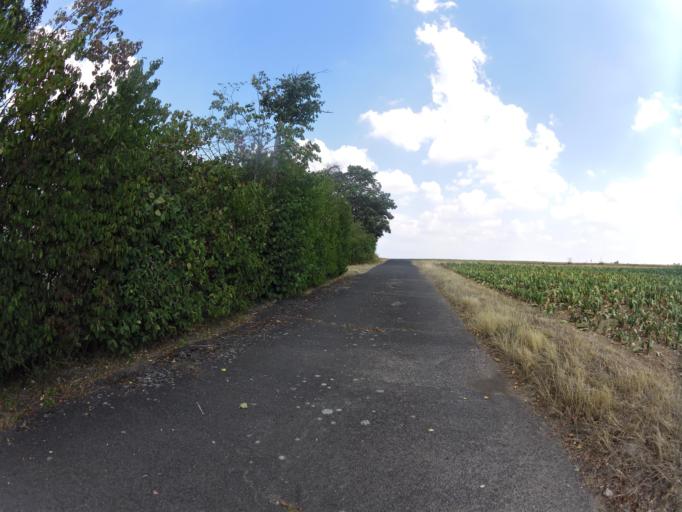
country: DE
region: Bavaria
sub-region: Regierungsbezirk Unterfranken
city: Ochsenfurt
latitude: 49.6408
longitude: 10.0631
